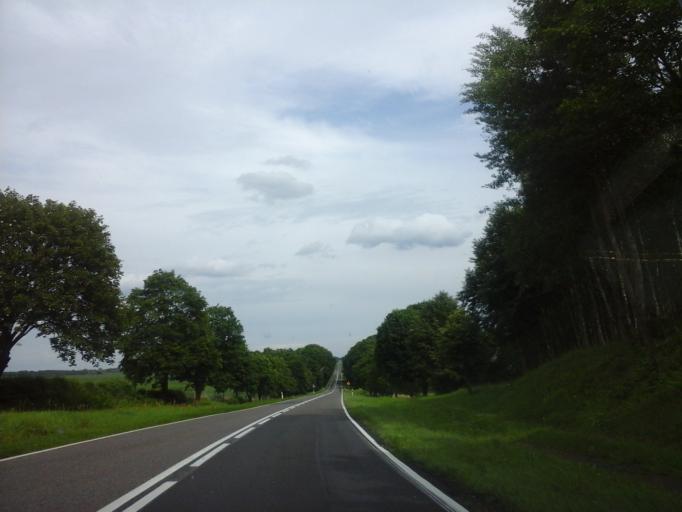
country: PL
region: West Pomeranian Voivodeship
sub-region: Powiat stargardzki
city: Suchan
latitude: 53.2757
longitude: 15.3868
